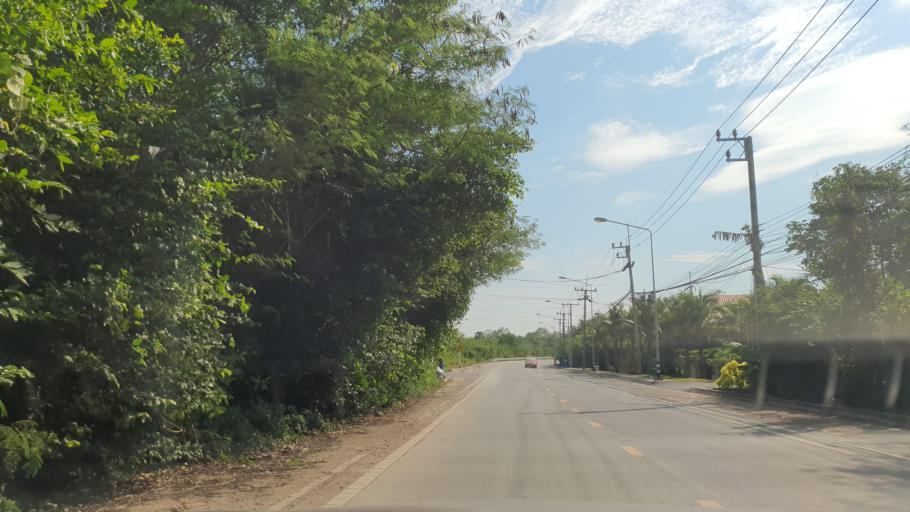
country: TH
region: Chon Buri
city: Phatthaya
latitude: 12.8040
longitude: 100.9260
